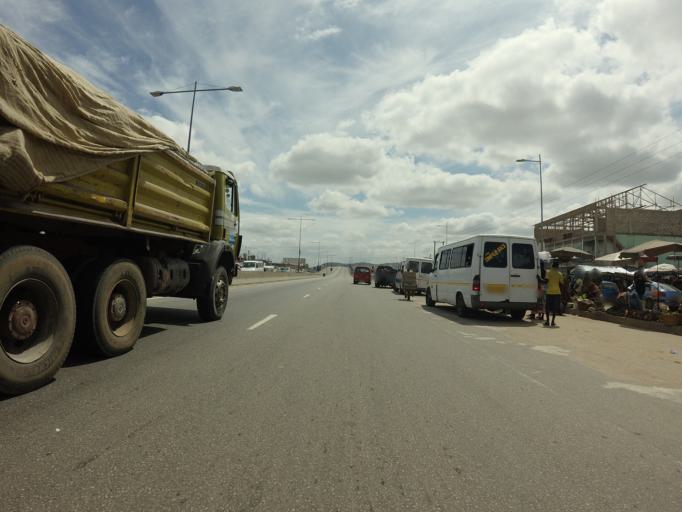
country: GH
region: Central
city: Kasoa
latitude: 5.5337
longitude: -0.4289
